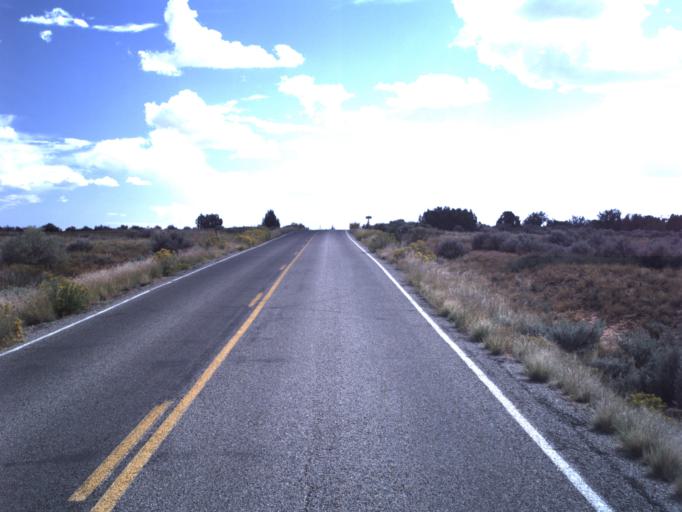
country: US
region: Utah
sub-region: Grand County
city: Moab
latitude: 38.5060
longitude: -109.7302
